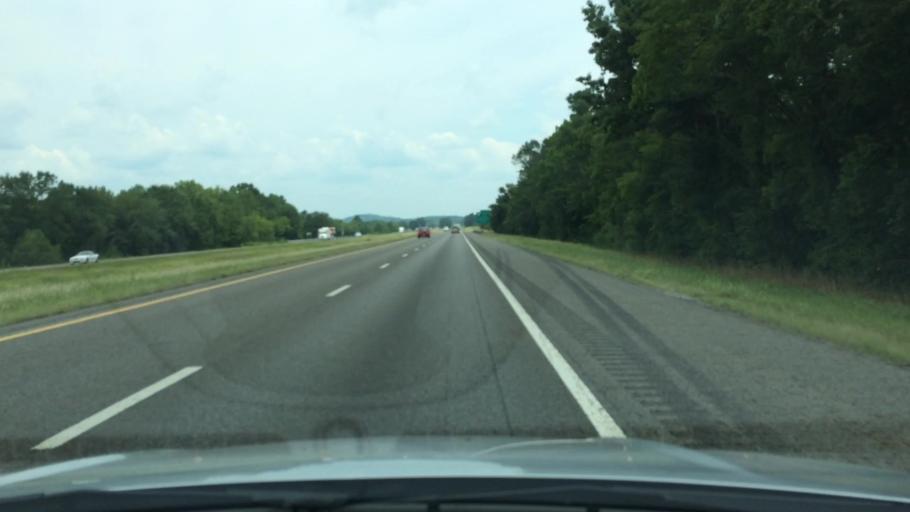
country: US
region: Tennessee
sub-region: Marshall County
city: Cornersville
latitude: 35.4309
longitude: -86.8797
